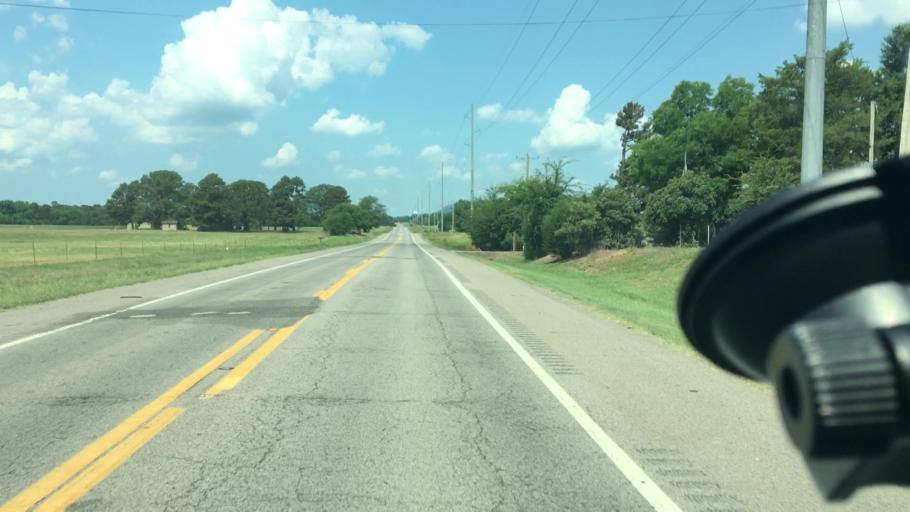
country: US
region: Arkansas
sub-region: Logan County
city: Paris
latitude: 35.2948
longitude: -93.6645
